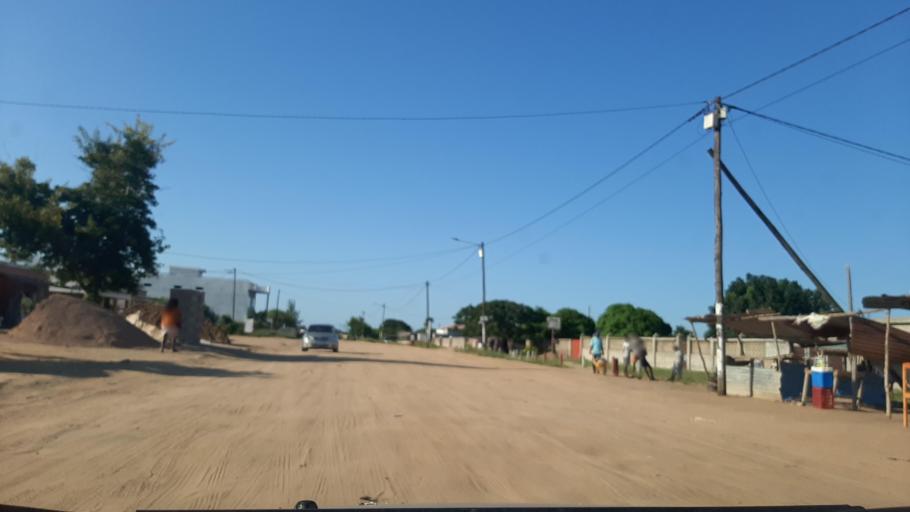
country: MZ
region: Maputo City
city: Maputo
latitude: -25.8074
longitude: 32.5464
